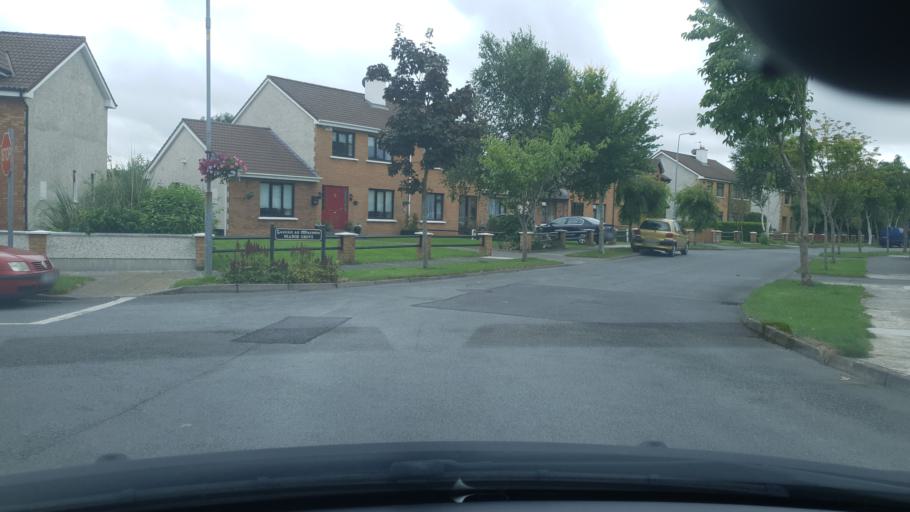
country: IE
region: Munster
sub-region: Ciarrai
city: Tralee
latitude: 52.2582
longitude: -9.6831
